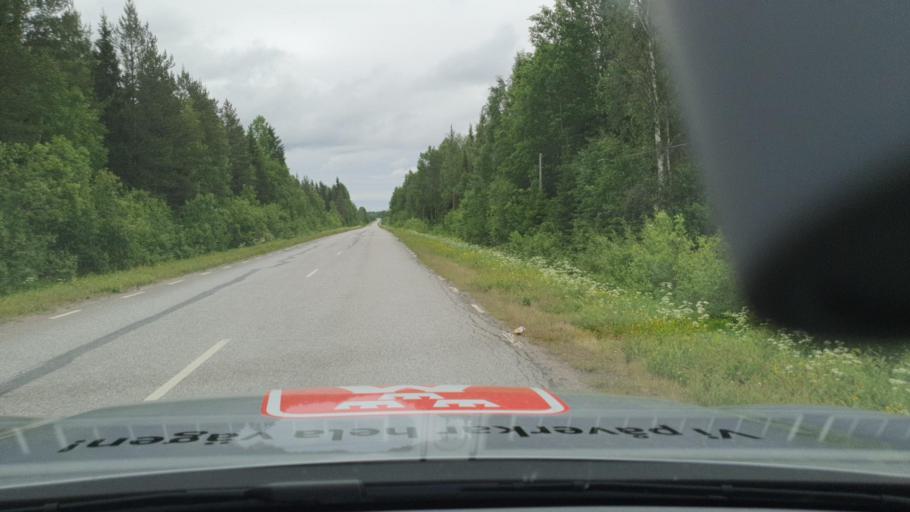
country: SE
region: Norrbotten
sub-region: Lulea Kommun
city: Ranea
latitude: 65.8536
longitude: 22.2389
